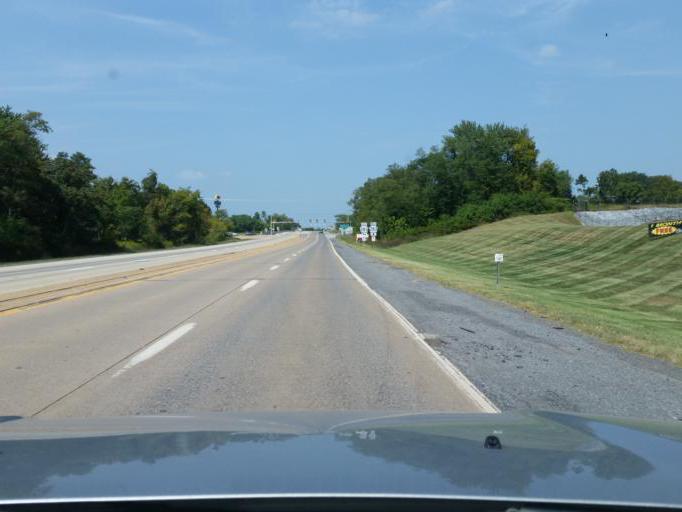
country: US
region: Pennsylvania
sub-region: Dauphin County
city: Middletown
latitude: 40.2197
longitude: -76.7190
